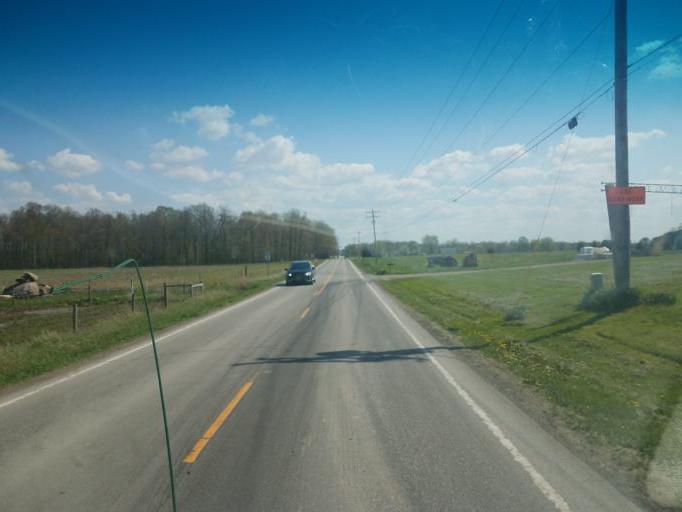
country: US
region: Ohio
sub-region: Wayne County
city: West Salem
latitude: 40.9319
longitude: -82.1092
